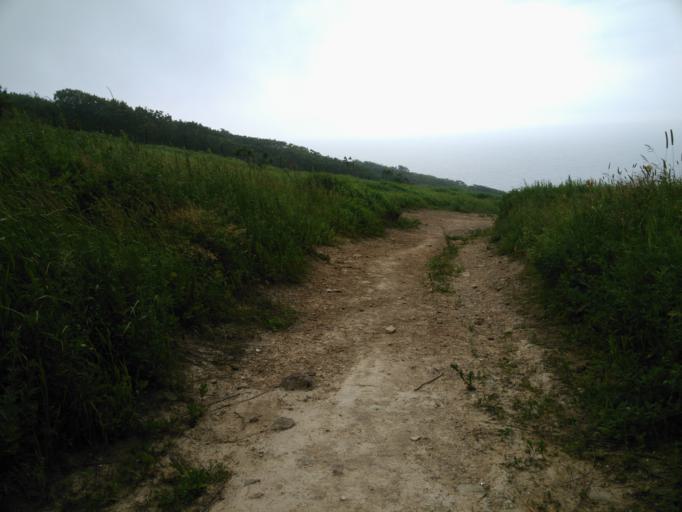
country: RU
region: Primorskiy
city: Vladivostok
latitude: 43.0951
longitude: 131.9870
